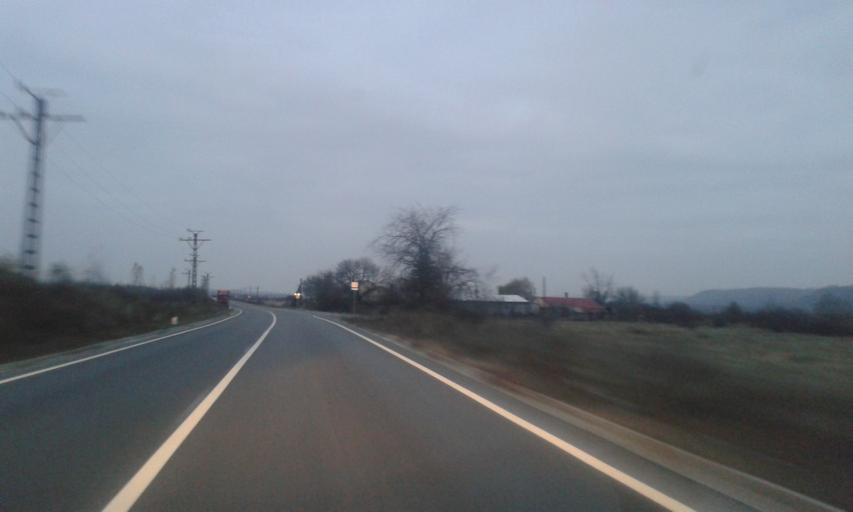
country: RO
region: Gorj
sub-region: Comuna Bumbesti-Jiu
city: Bumbesti-Jiu
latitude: 45.1571
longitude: 23.3752
